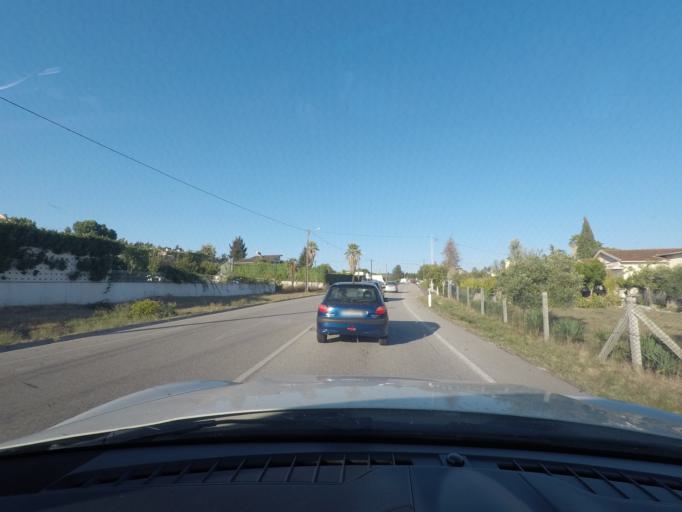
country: PT
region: Coimbra
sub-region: Vila Nova de Poiares
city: Poiares
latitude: 40.1806
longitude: -8.2636
